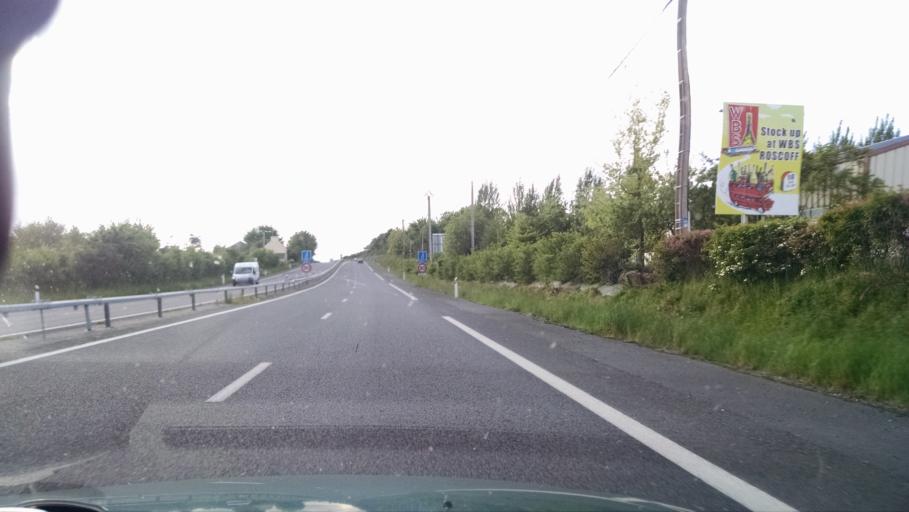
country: FR
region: Brittany
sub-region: Departement du Finistere
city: Henvic
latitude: 48.6433
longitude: -3.9370
